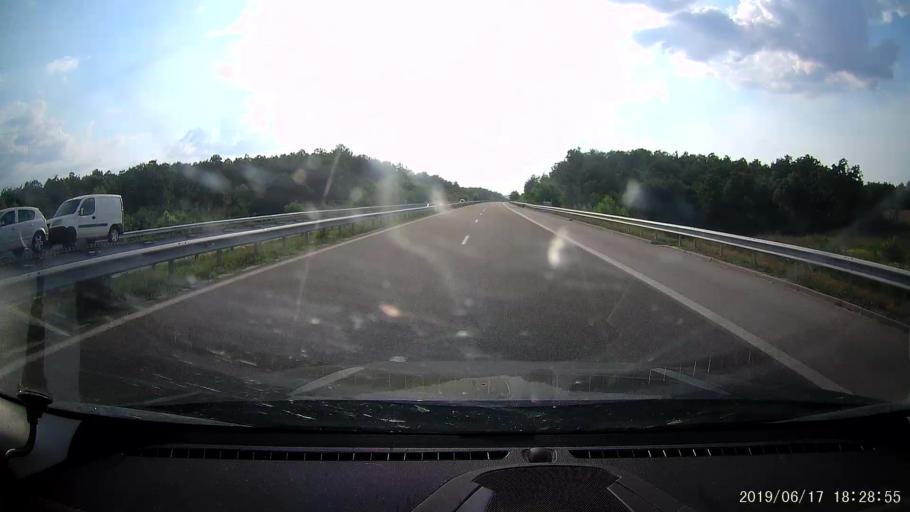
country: BG
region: Khaskovo
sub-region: Obshtina Dimitrovgrad
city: Dimitrovgrad
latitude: 42.0251
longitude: 25.5680
